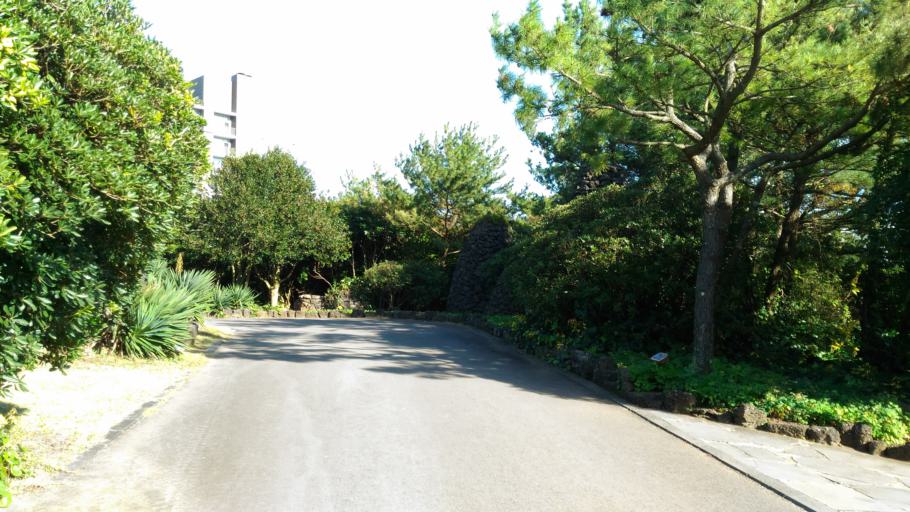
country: KR
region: Jeju-do
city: Seogwipo
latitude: 33.3207
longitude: 126.8432
